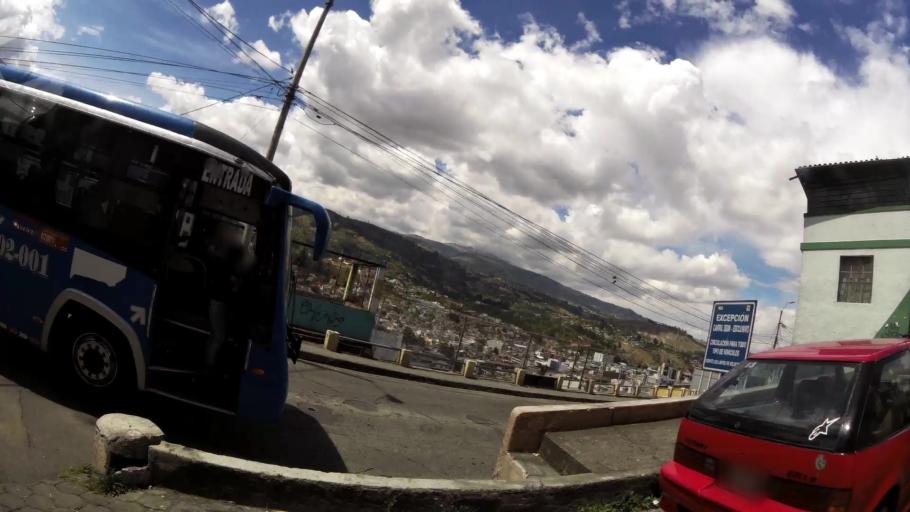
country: EC
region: Tungurahua
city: Ambato
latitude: -1.2473
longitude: -78.6312
